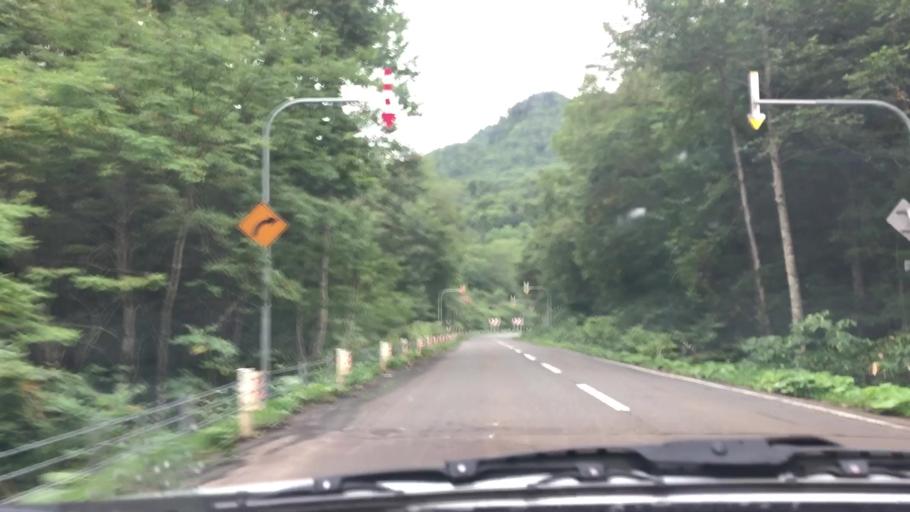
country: JP
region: Hokkaido
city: Shimo-furano
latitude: 42.9170
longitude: 142.3740
